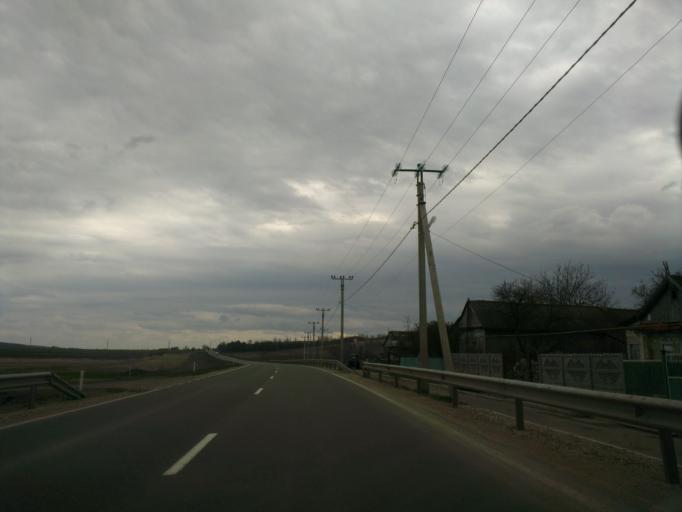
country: MD
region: Cimislia
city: Cimislia
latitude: 46.6120
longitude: 28.7280
